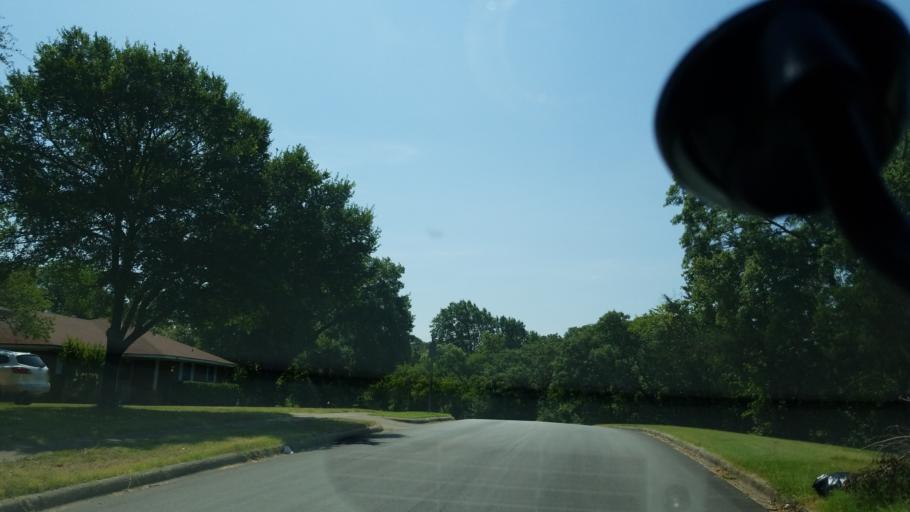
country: US
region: Texas
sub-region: Dallas County
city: Cockrell Hill
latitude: 32.7079
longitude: -96.8781
